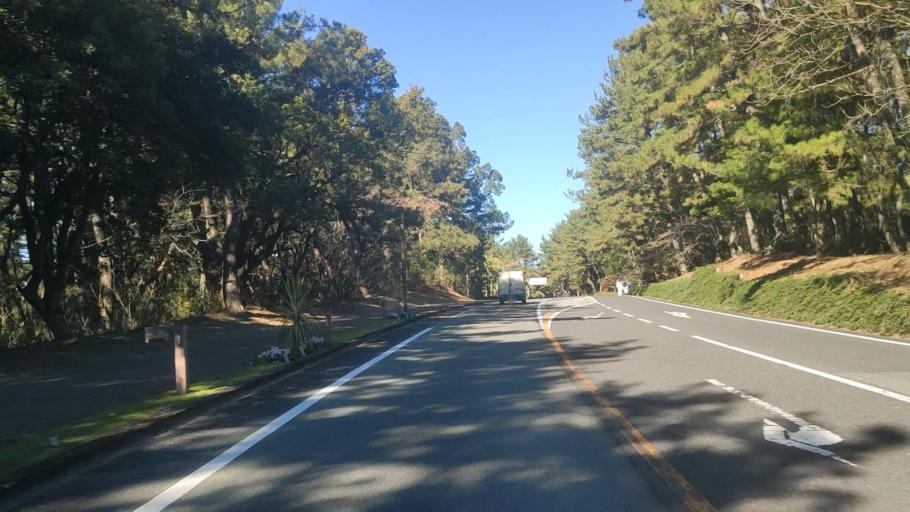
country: JP
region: Miyazaki
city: Miyazaki-shi
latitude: 31.9561
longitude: 131.4671
